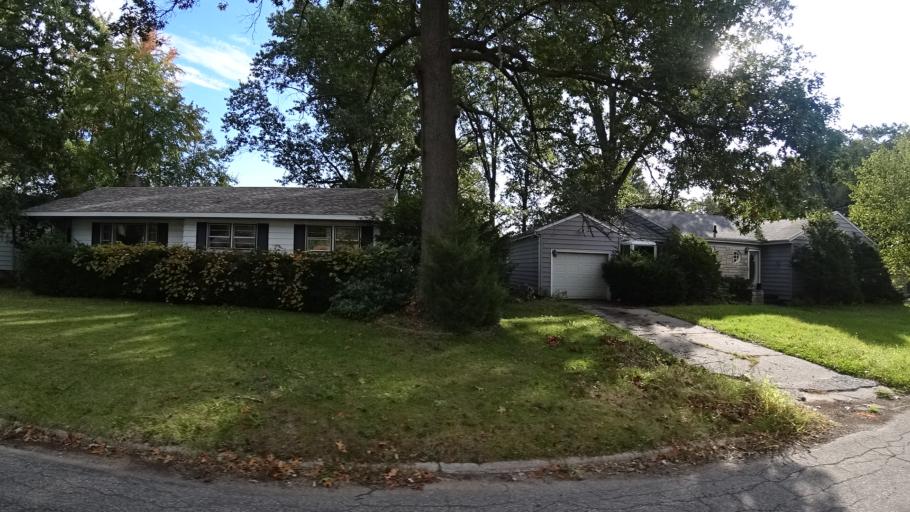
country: US
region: Indiana
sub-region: LaPorte County
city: Trail Creek
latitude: 41.7029
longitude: -86.8726
